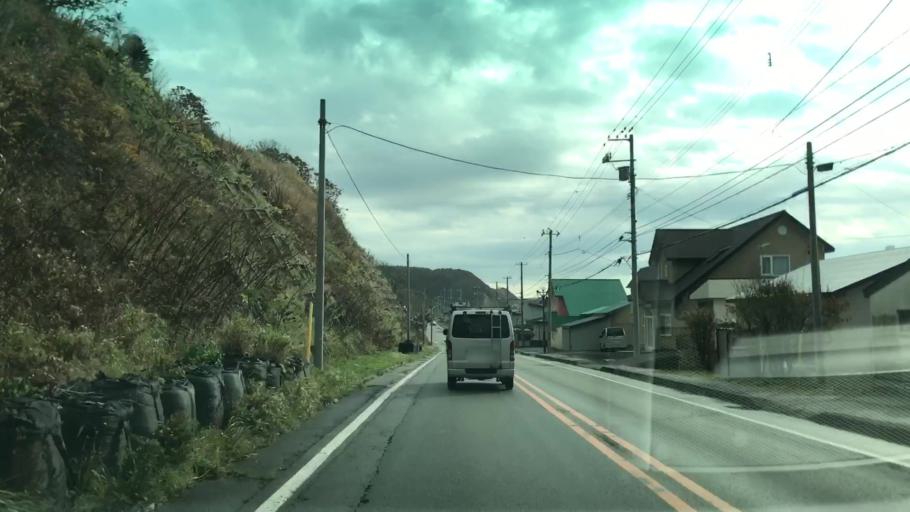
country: JP
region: Hokkaido
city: Shizunai-furukawacho
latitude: 42.1527
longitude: 142.7973
